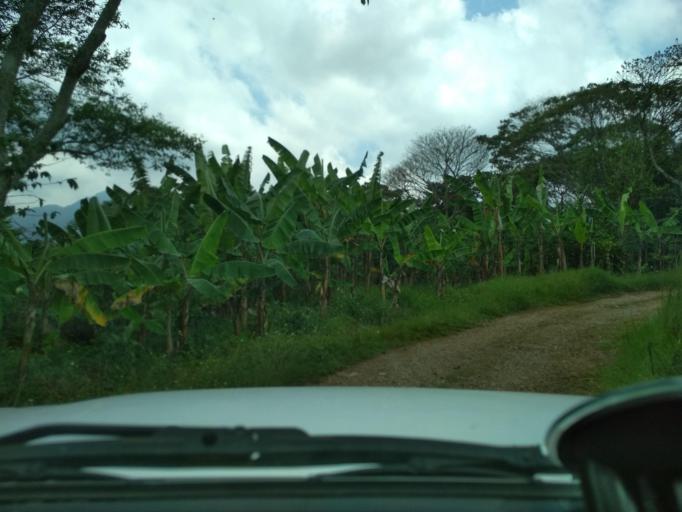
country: MX
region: Veracruz
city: Tocuila
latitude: 18.9493
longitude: -97.0193
